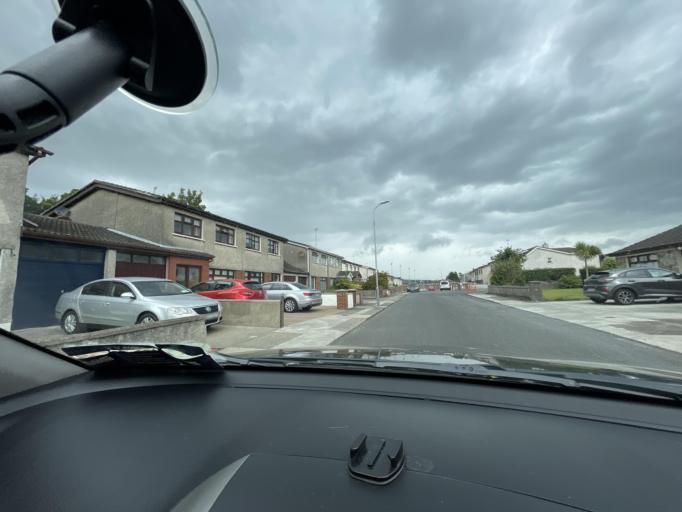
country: IE
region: Leinster
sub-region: Lu
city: Drogheda
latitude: 53.7216
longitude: -6.3574
